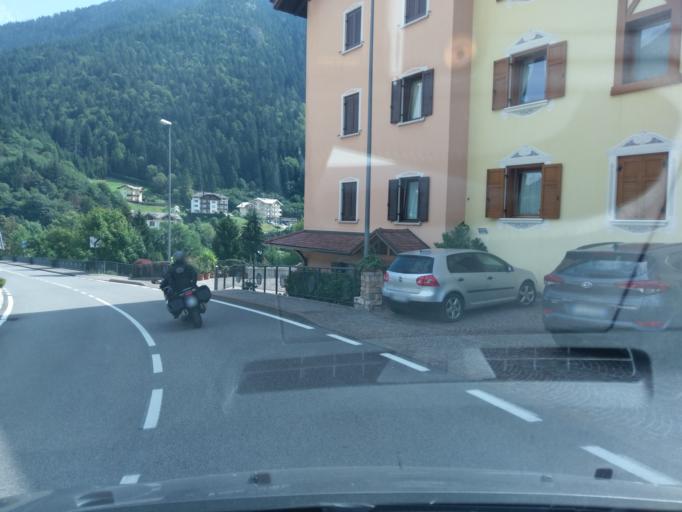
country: IT
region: Trentino-Alto Adige
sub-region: Provincia di Trento
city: Molveno
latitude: 46.1409
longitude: 10.9660
